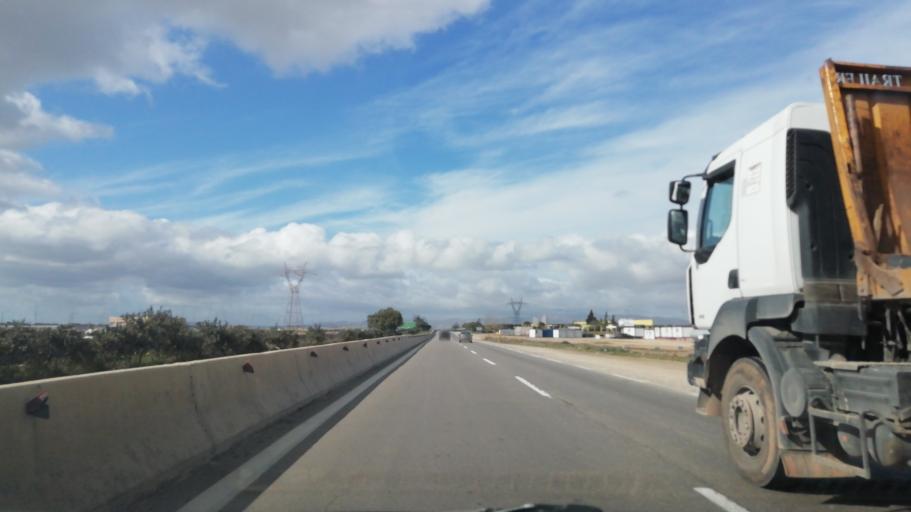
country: DZ
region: Oran
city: Ain el Bya
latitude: 35.7764
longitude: -0.2579
